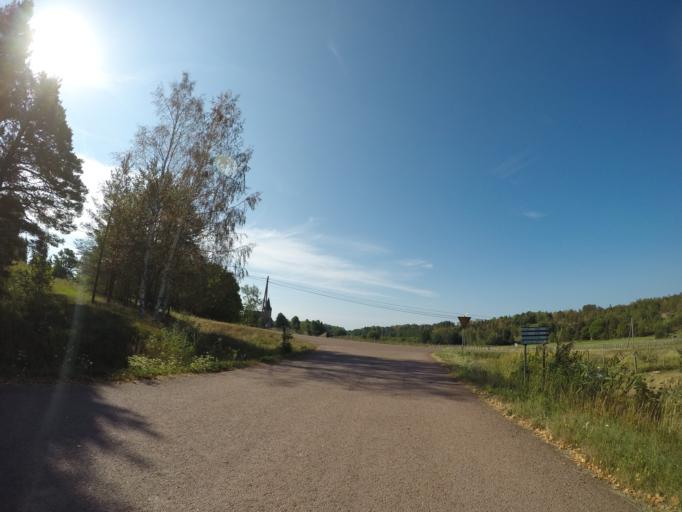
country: AX
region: Alands landsbygd
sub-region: Finstroem
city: Finstroem
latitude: 60.2665
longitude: 19.9294
